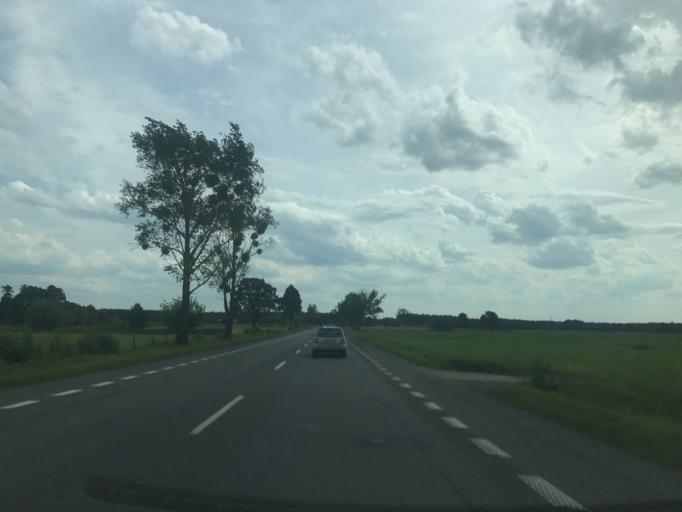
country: PL
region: Masovian Voivodeship
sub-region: Powiat mlawski
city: Strzegowo
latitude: 52.9373
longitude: 20.2834
